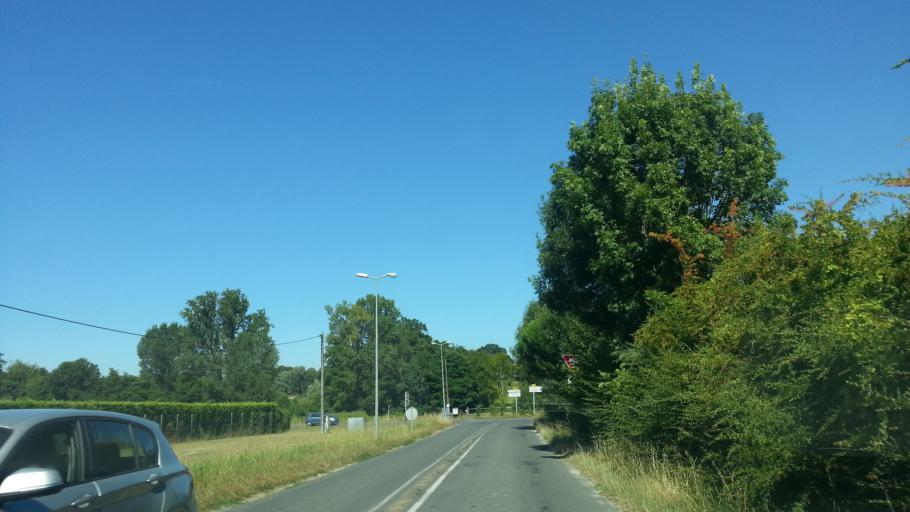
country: FR
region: Aquitaine
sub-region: Departement de la Gironde
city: Martillac
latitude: 44.6915
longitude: -0.5121
